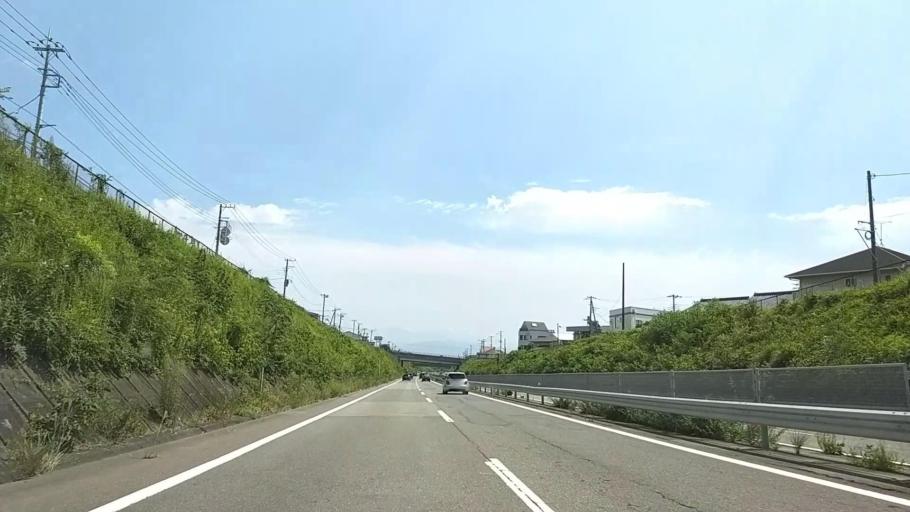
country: JP
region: Shizuoka
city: Fuji
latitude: 35.1942
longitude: 138.6701
